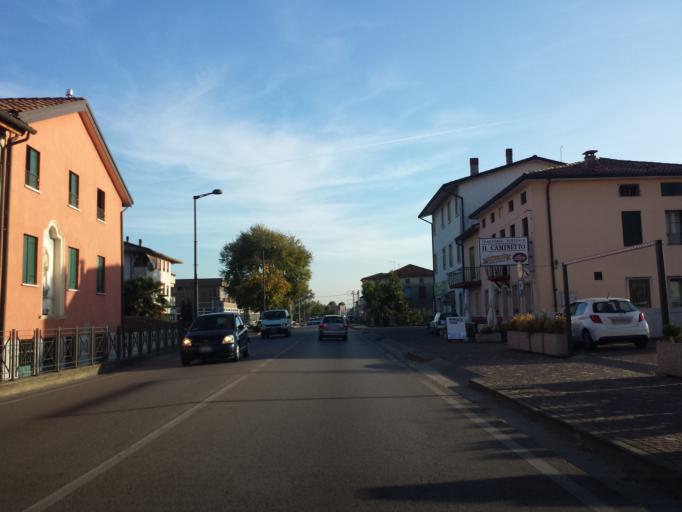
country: IT
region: Veneto
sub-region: Provincia di Vicenza
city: Motta
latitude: 45.5972
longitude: 11.4960
